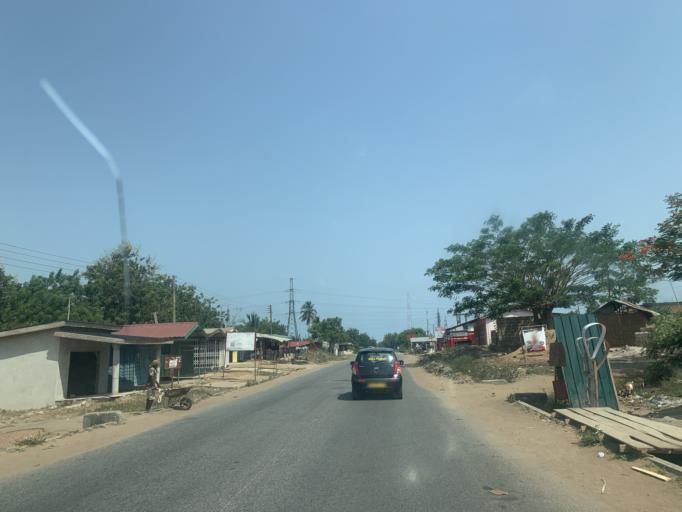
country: GH
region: Central
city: Winneba
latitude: 5.3904
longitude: -0.6460
